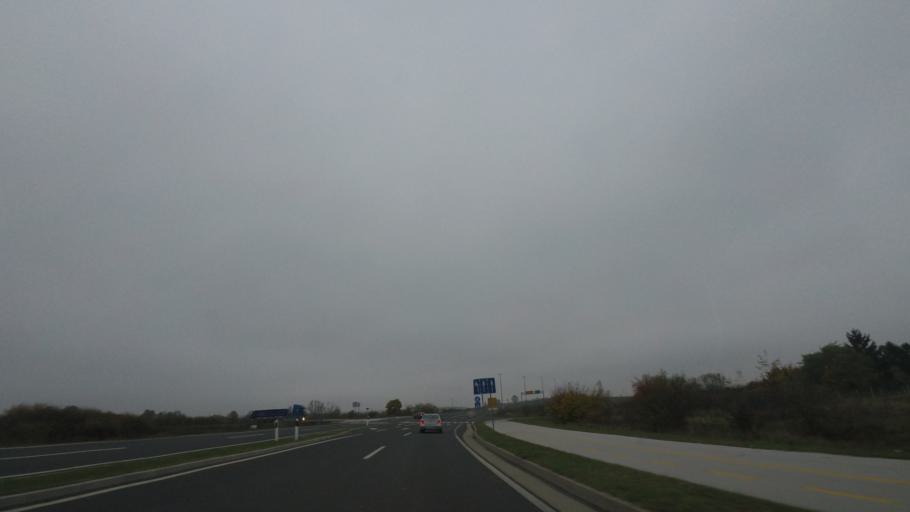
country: HR
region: Zagrebacka
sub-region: Grad Velika Gorica
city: Velika Gorica
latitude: 45.6930
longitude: 16.0767
